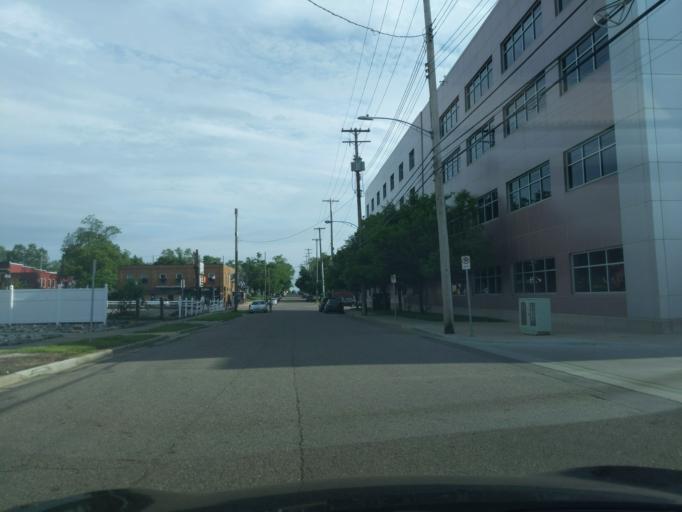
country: US
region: Michigan
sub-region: Ingham County
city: Lansing
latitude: 42.7344
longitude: -84.5411
